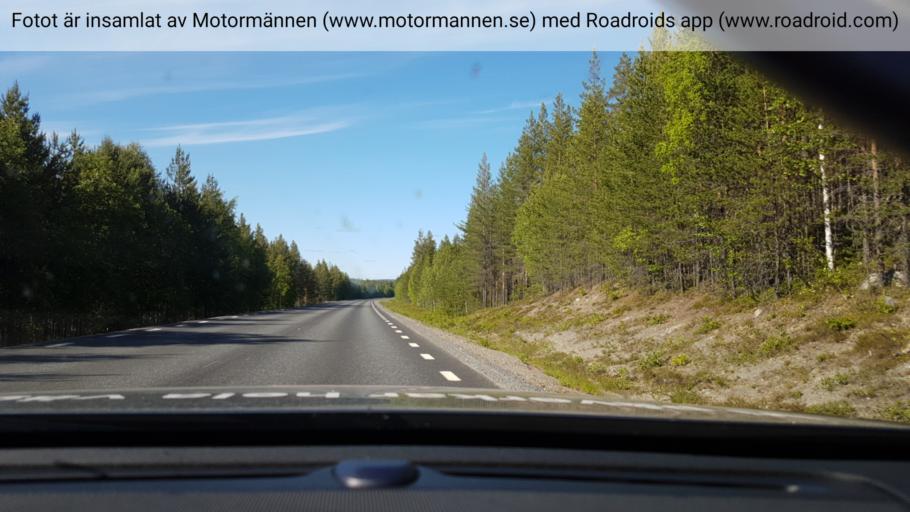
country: SE
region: Vaesterbotten
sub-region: Lycksele Kommun
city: Lycksele
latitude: 64.7948
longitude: 18.7318
